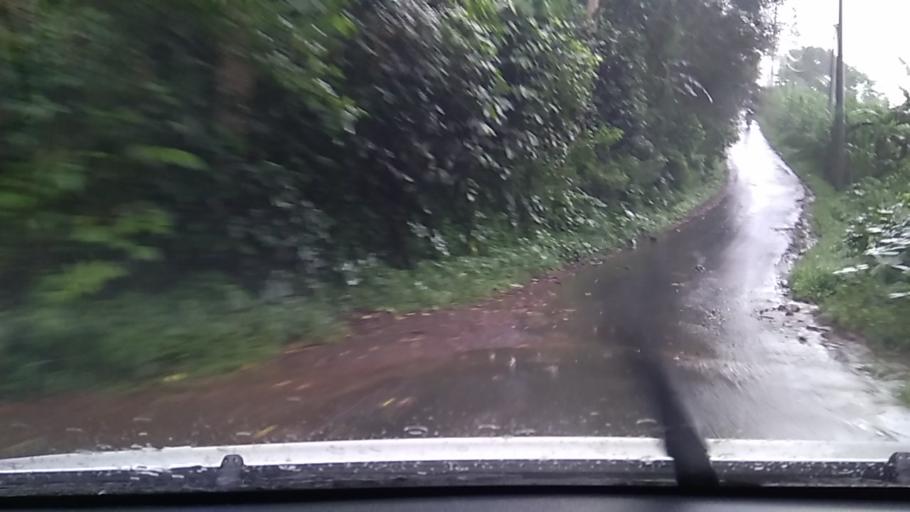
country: ID
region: Bali
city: Banjar Ambengan
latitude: -8.2207
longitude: 115.1627
